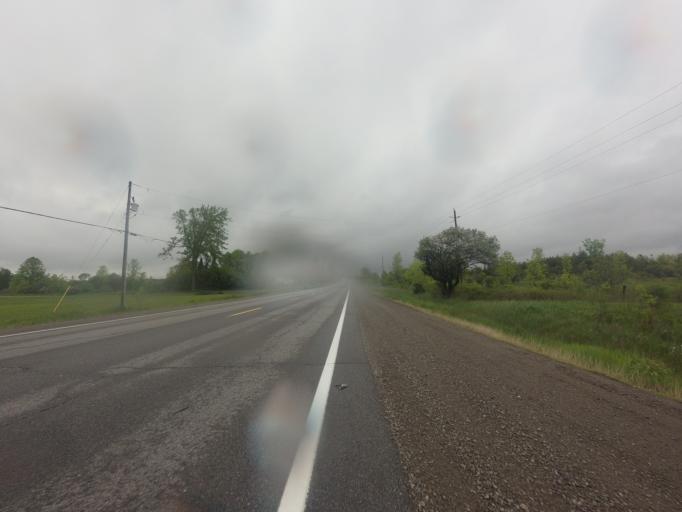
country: CA
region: Ontario
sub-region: Lanark County
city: Smiths Falls
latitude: 44.8580
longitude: -76.0534
